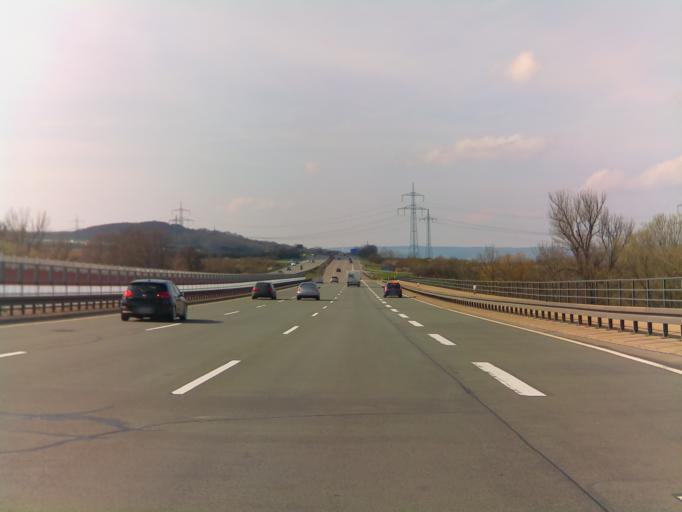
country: DE
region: Thuringia
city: Mellingen
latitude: 50.9283
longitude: 11.3947
